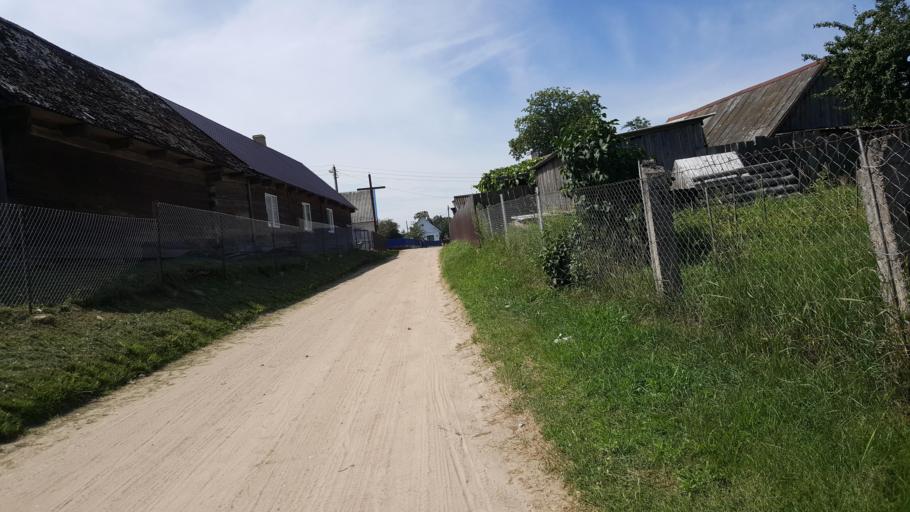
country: BY
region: Brest
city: Pruzhany
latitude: 52.5518
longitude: 24.2199
